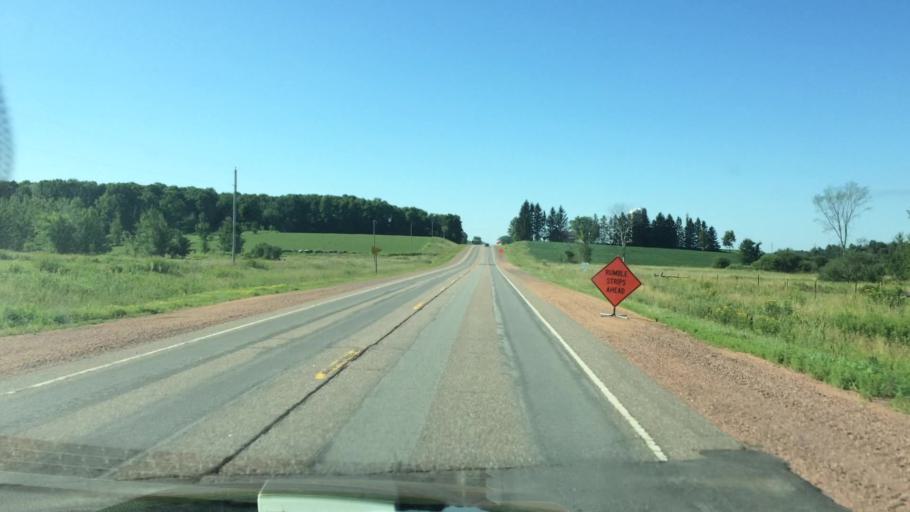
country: US
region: Wisconsin
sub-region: Marathon County
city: Stratford
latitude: 44.9138
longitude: -90.0787
